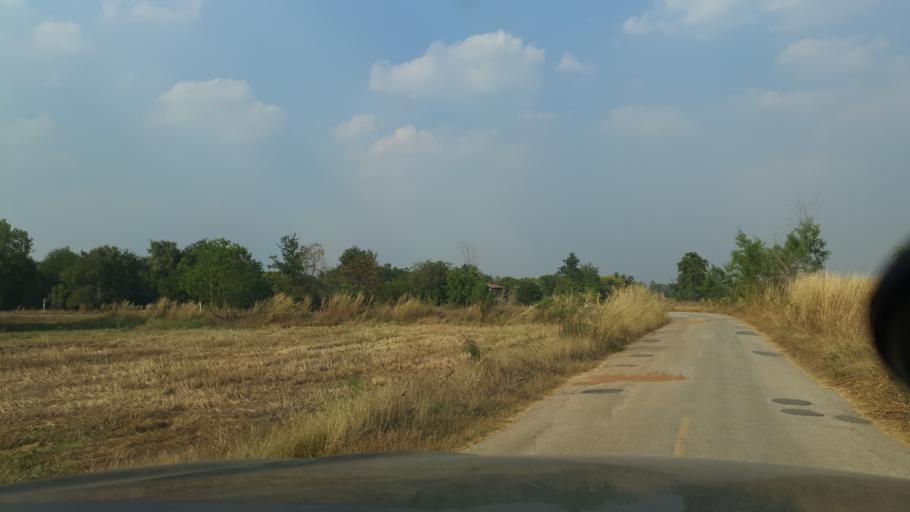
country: TH
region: Sukhothai
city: Ban Dan Lan Hoi
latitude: 17.0224
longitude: 99.5554
